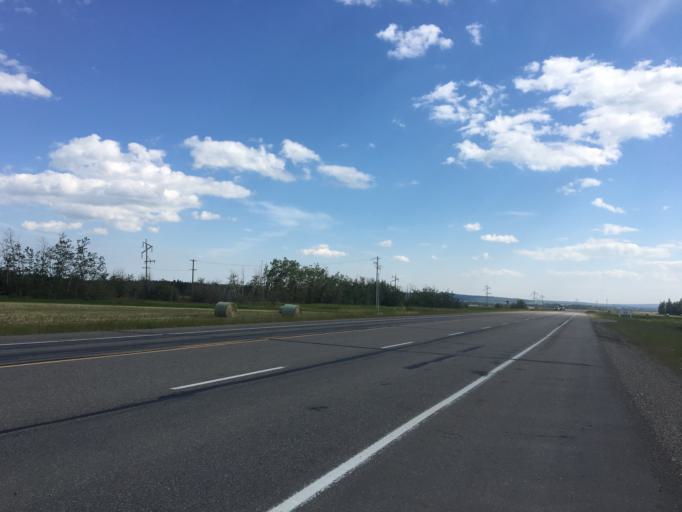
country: CA
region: Alberta
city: Spirit River
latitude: 55.6343
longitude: -118.7005
